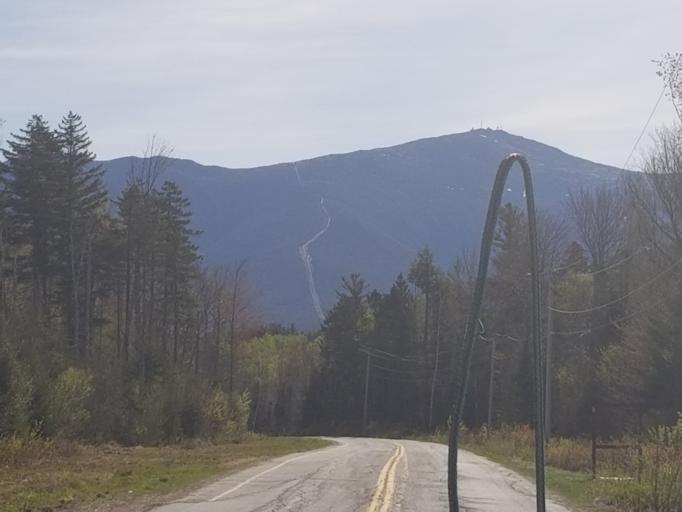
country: US
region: New Hampshire
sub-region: Coos County
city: Jefferson
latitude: 44.2558
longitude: -71.4536
